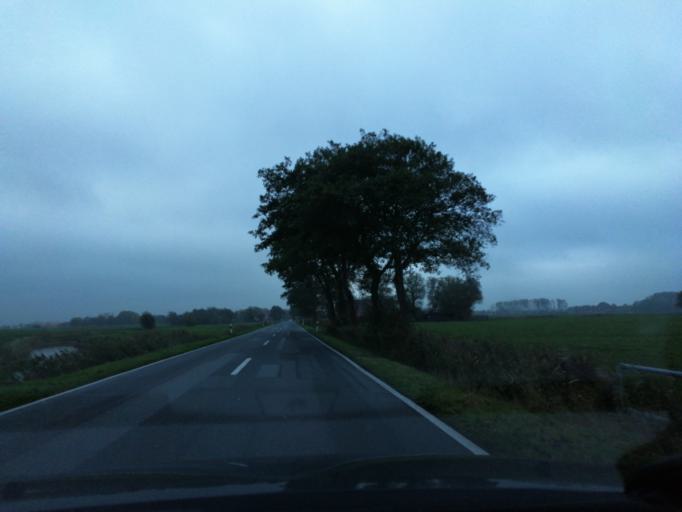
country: DE
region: Lower Saxony
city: Jever
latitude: 53.6672
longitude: 7.8642
